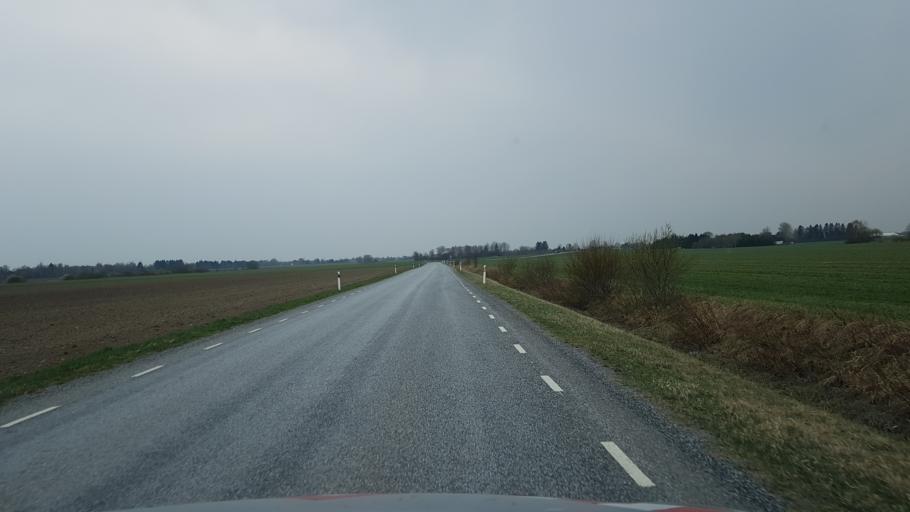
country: EE
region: Harju
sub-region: Saue linn
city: Saue
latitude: 59.3370
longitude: 24.5741
